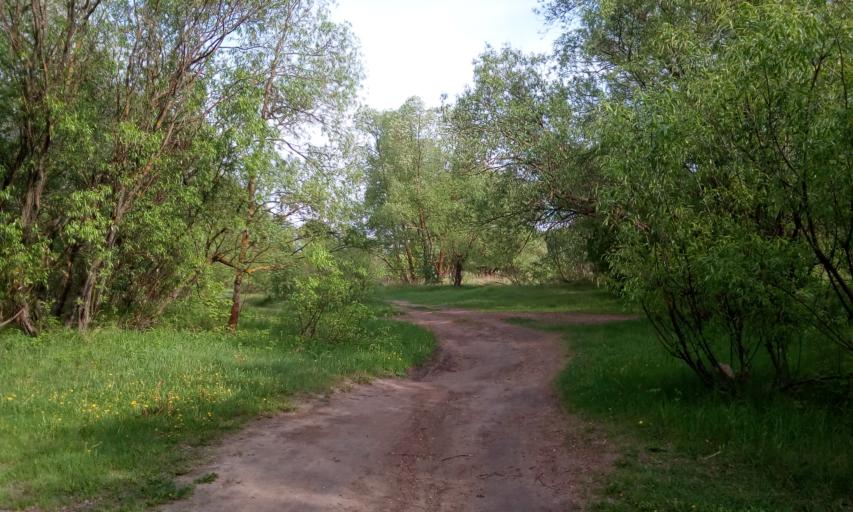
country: RU
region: Penza
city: Penza
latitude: 53.1674
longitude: 45.0417
